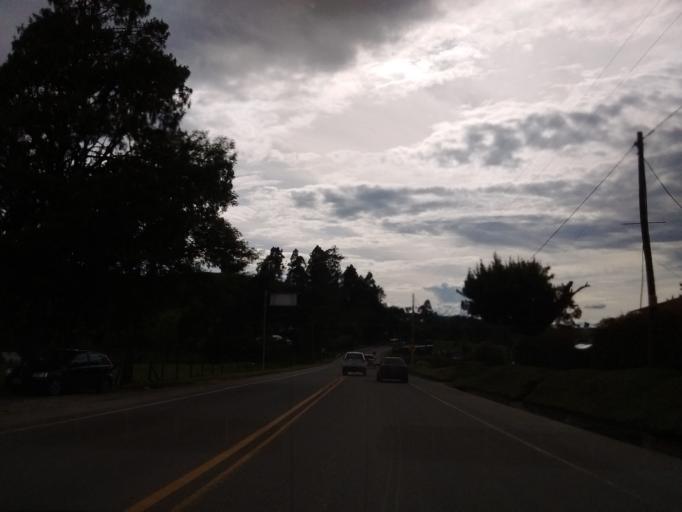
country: CO
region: Antioquia
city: Santuario
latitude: 6.1251
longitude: -75.2461
